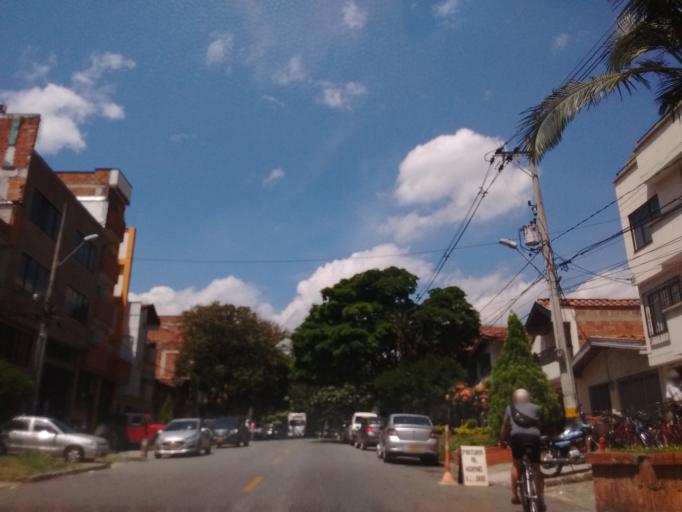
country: CO
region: Antioquia
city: Medellin
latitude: 6.2497
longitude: -75.6049
